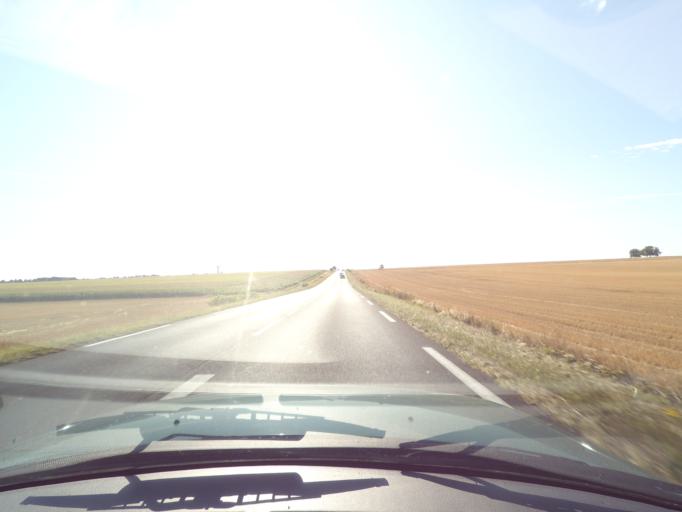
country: FR
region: Poitou-Charentes
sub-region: Departement de la Vienne
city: Cisse
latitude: 46.6344
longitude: 0.2288
